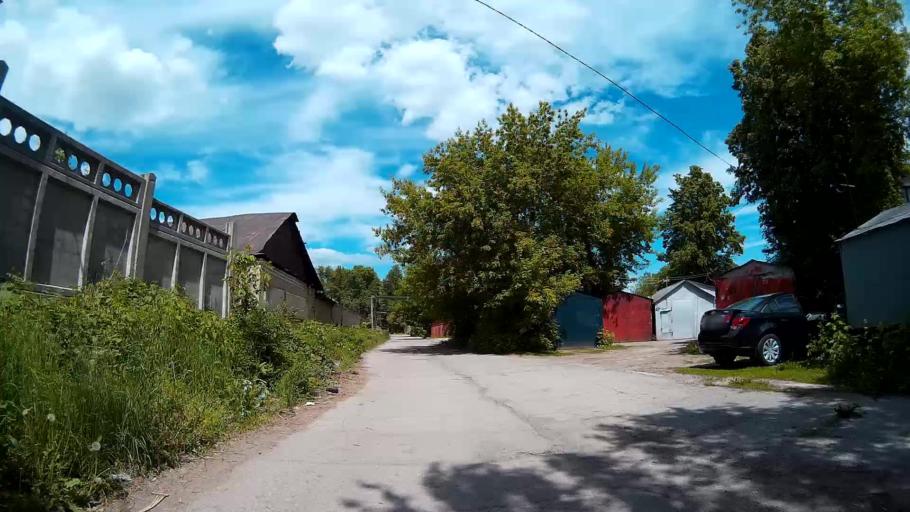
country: RU
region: Ulyanovsk
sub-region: Ulyanovskiy Rayon
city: Ulyanovsk
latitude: 54.2857
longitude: 48.3669
